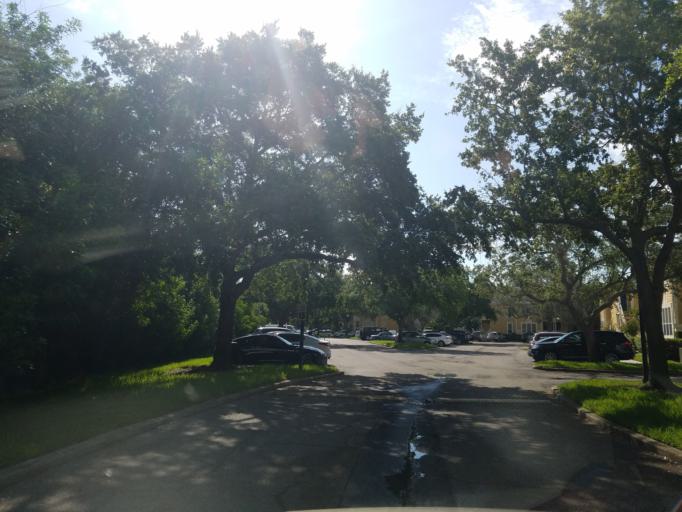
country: US
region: Florida
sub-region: Pinellas County
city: Gandy
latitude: 27.8756
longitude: -82.6343
